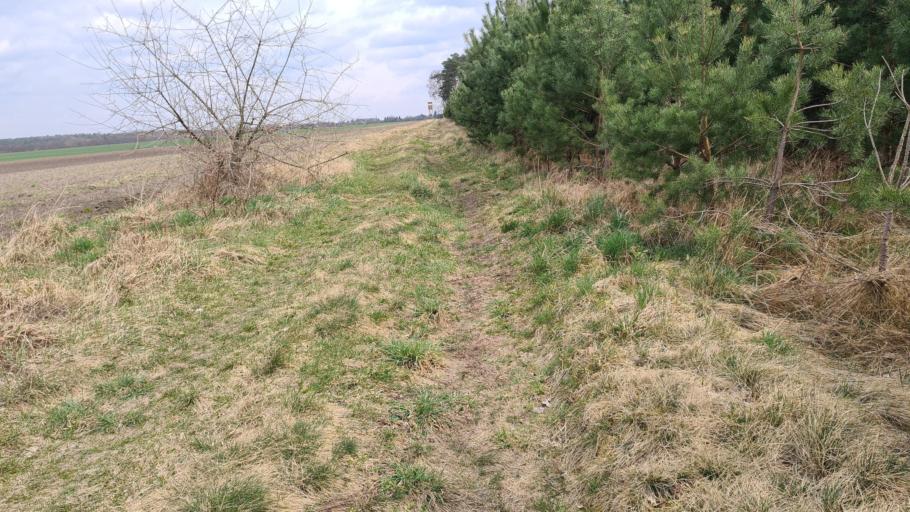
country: DE
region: Brandenburg
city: Ruckersdorf
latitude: 51.6027
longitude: 13.6276
